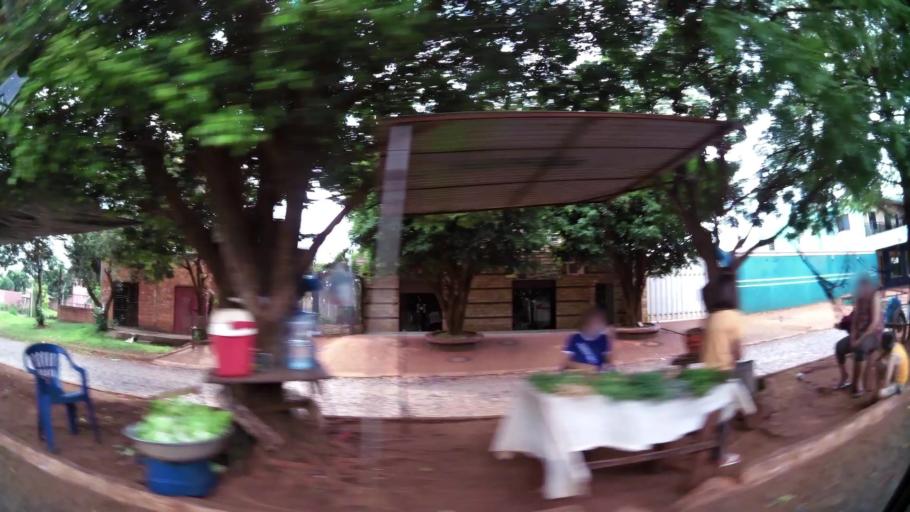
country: PY
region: Alto Parana
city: Presidente Franco
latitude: -25.5350
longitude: -54.6495
